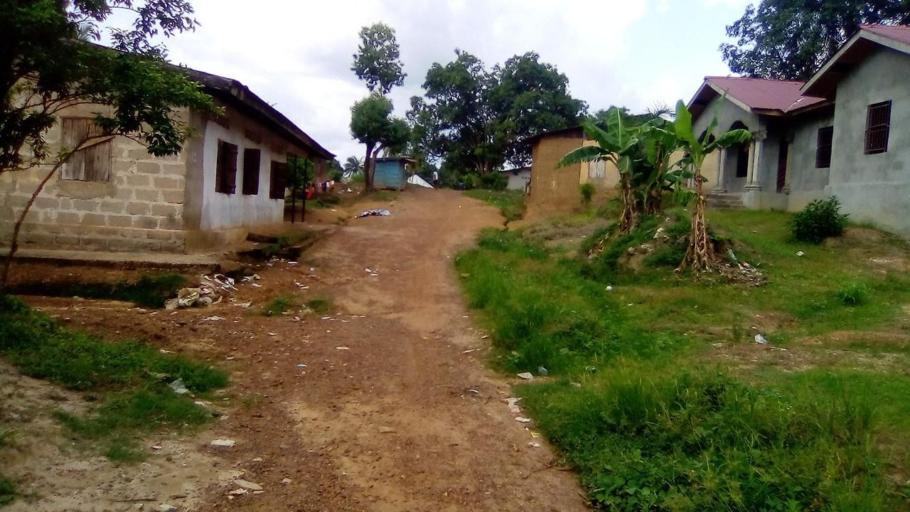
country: SL
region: Southern Province
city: Bo
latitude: 7.9591
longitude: -11.7252
